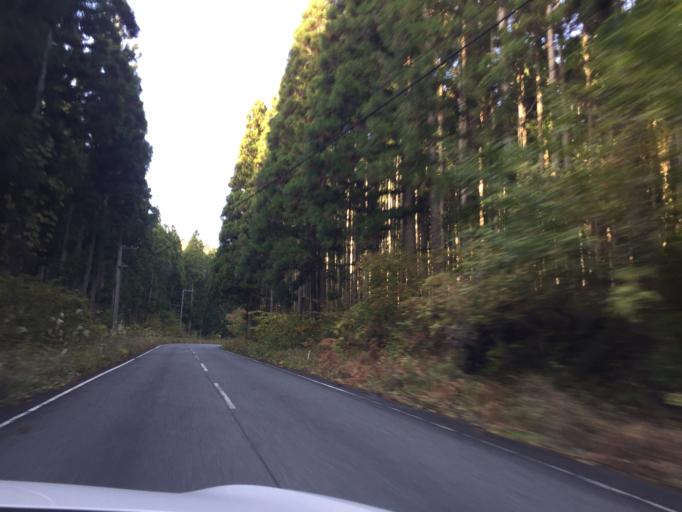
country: JP
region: Fukushima
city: Iwaki
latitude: 37.2384
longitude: 140.7629
